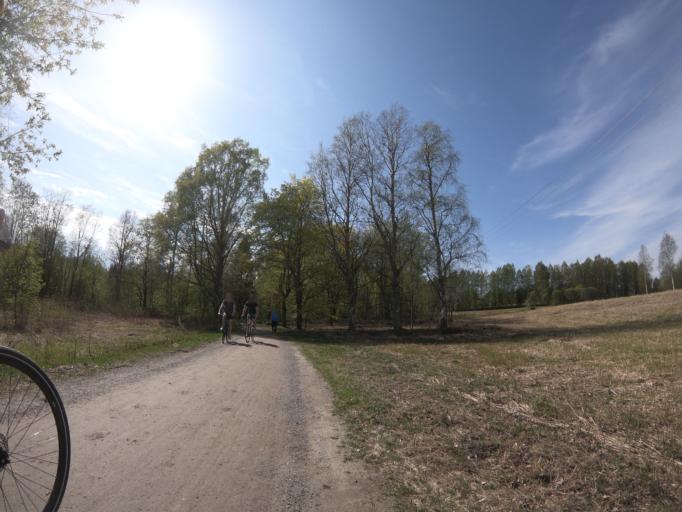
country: SE
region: Vaesterbotten
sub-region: Umea Kommun
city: Roback
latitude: 63.8296
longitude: 20.1798
